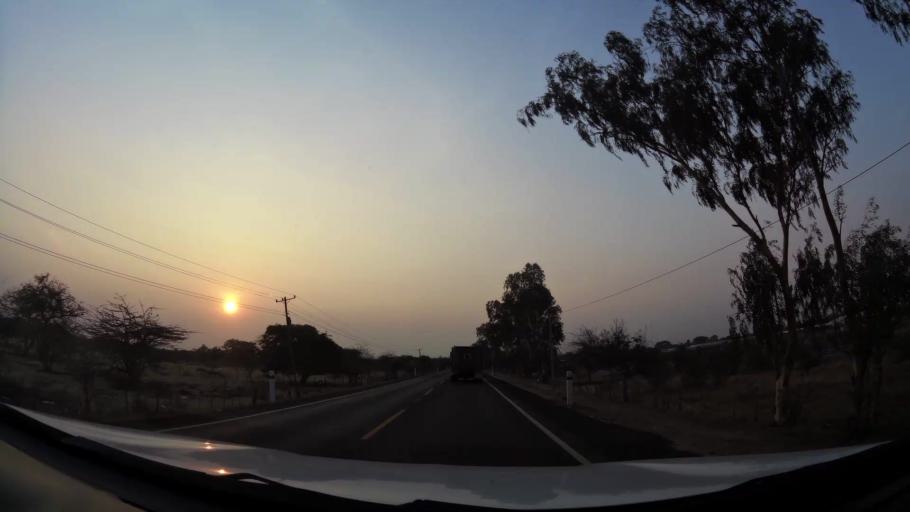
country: NI
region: Leon
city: La Paz Centro
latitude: 12.3026
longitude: -86.7747
